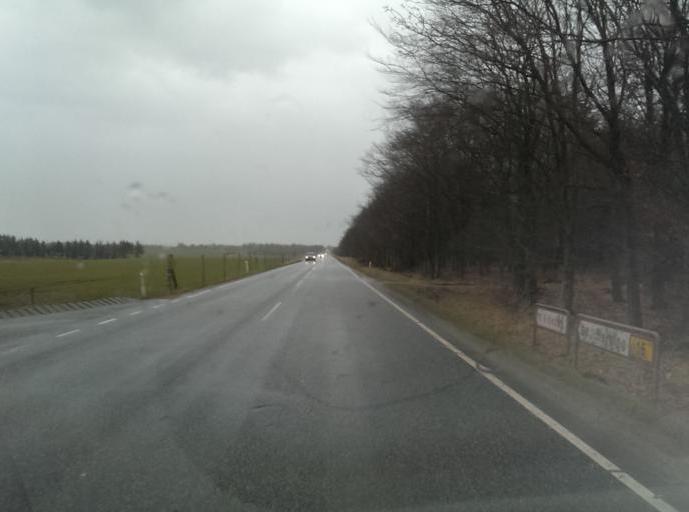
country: DK
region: Central Jutland
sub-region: Ringkobing-Skjern Kommune
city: Skjern
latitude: 56.0836
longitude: 8.4452
